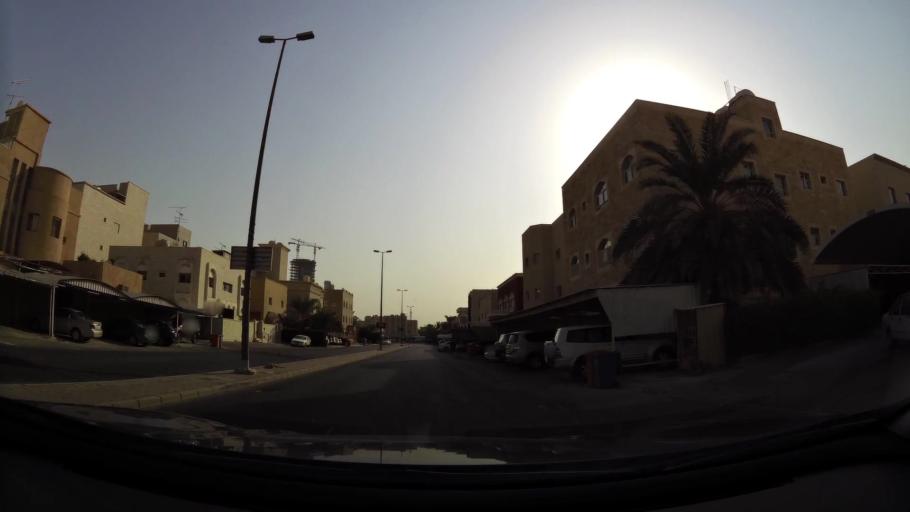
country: KW
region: Al Asimah
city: Ad Dasmah
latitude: 29.3658
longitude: 48.0034
